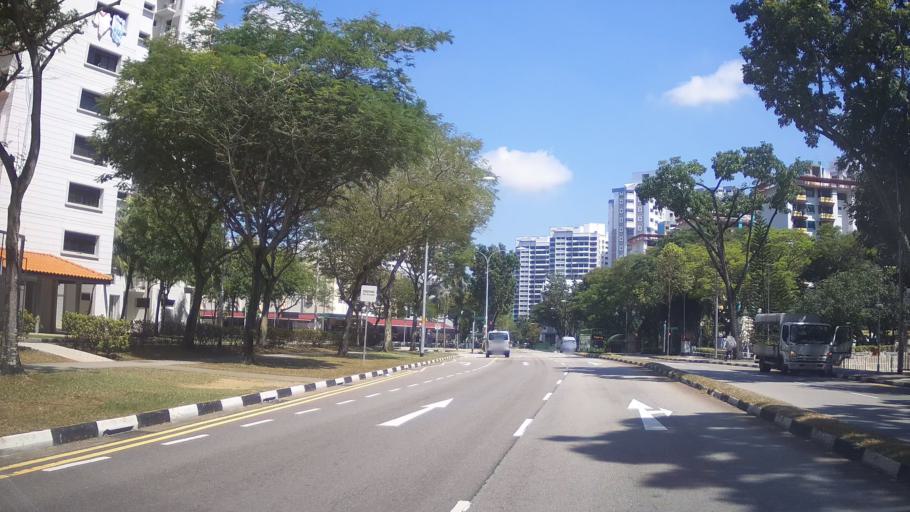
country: SG
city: Singapore
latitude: 1.3334
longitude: 103.7230
